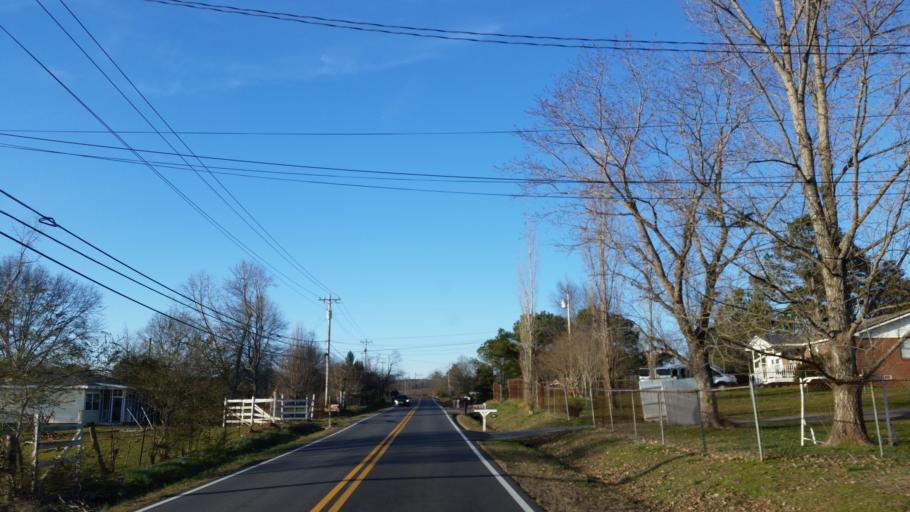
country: US
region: Georgia
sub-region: Gordon County
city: Calhoun
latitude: 34.5624
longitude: -84.9717
